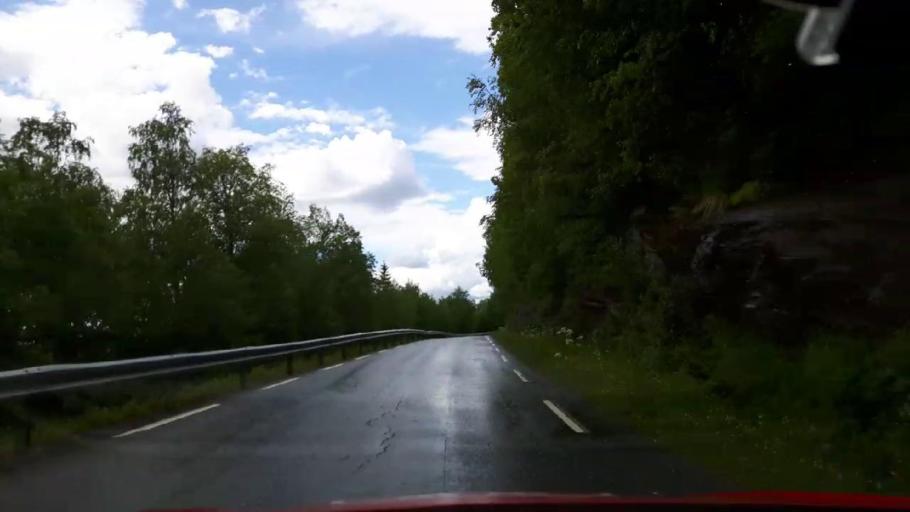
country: NO
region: Nord-Trondelag
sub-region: Lierne
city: Sandvika
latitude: 64.1065
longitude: 13.9864
